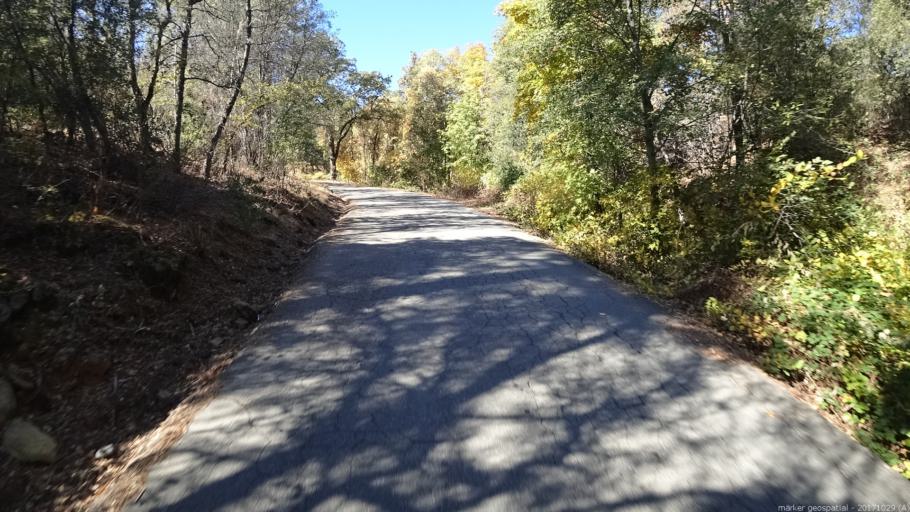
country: US
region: California
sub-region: Shasta County
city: Shasta
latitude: 40.4894
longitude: -122.6827
